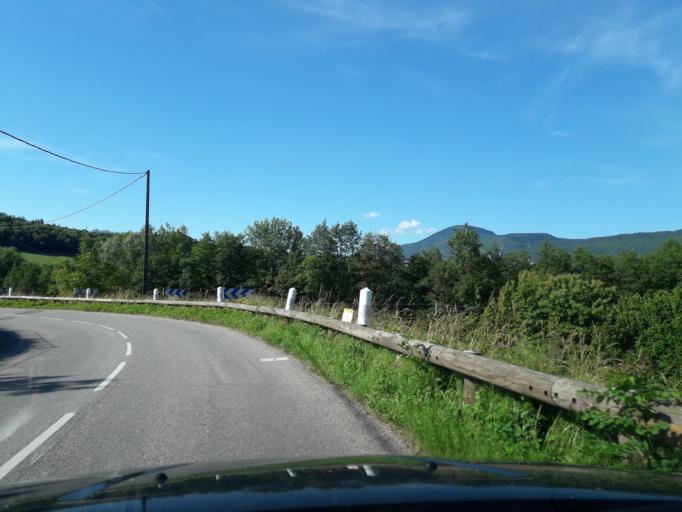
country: FR
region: Rhone-Alpes
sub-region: Departement de la Savoie
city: La Bridoire
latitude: 45.5415
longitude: 5.7723
